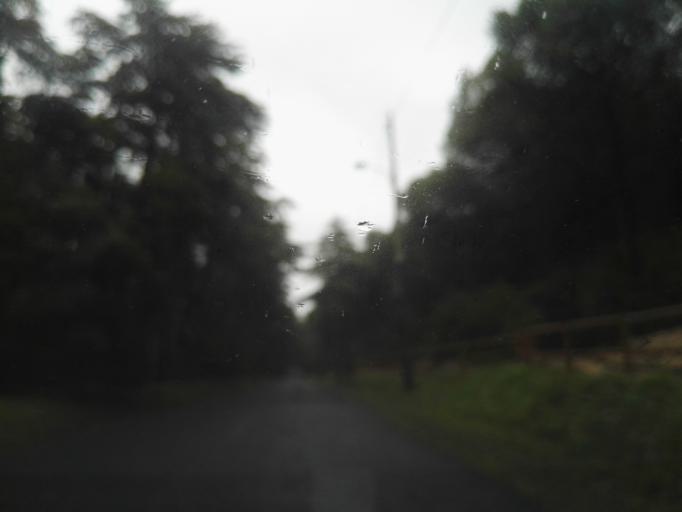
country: PT
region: Lisbon
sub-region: Odivelas
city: Pontinha
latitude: 38.7306
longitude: -9.1788
